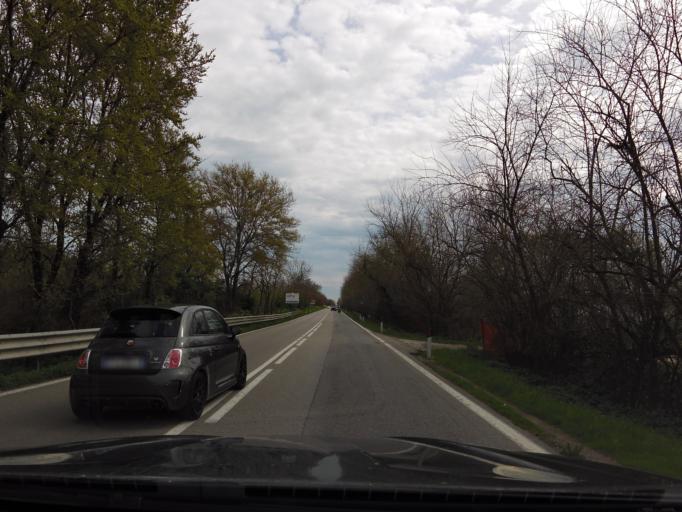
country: IT
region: The Marches
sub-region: Provincia di Macerata
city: Porto Recanati
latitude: 43.4171
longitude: 13.6678
